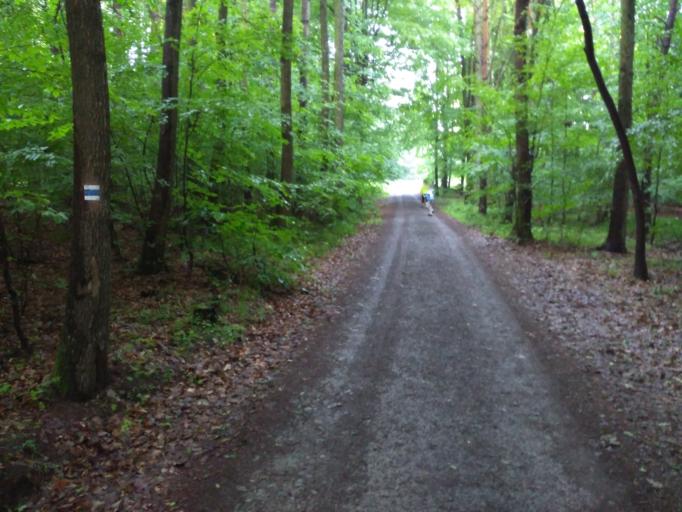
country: CZ
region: Central Bohemia
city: Hudlice
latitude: 49.9581
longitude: 13.9266
